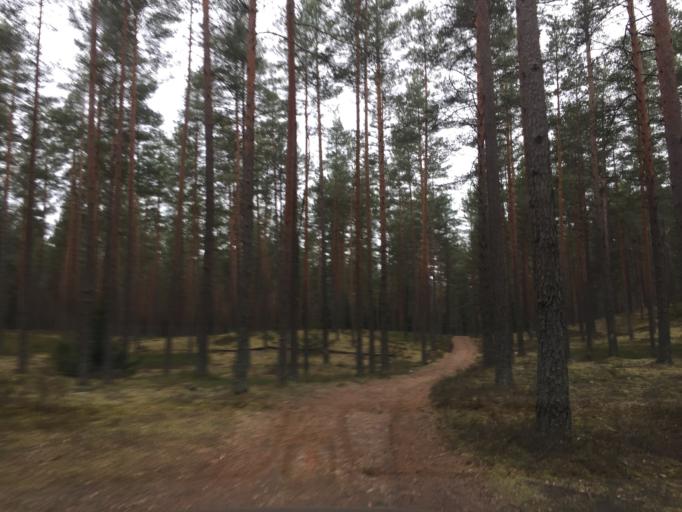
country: LV
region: Garkalne
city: Garkalne
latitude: 56.9646
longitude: 24.4384
